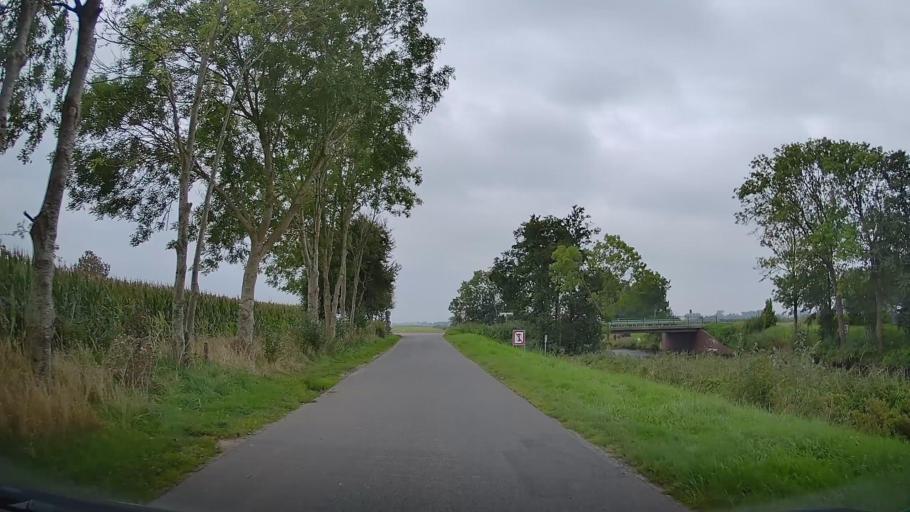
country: DE
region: Lower Saxony
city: Osterbruch
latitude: 53.8227
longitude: 8.9576
